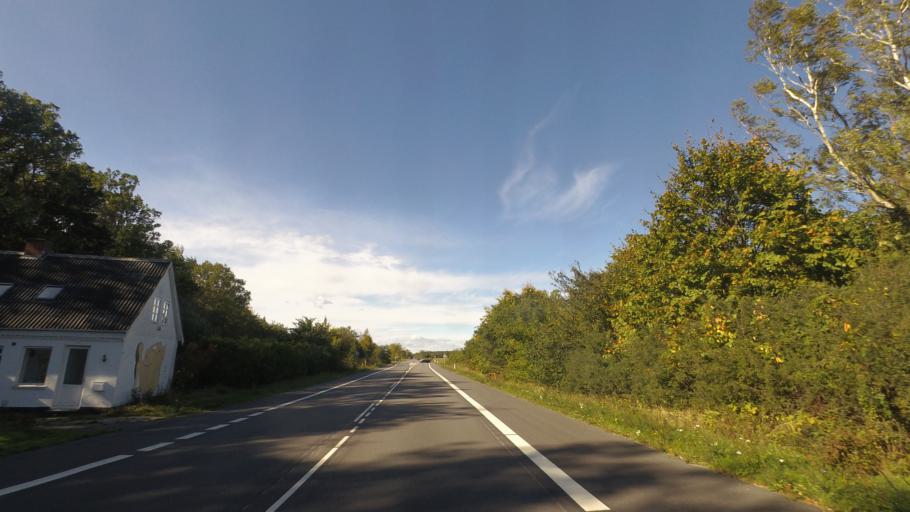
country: DK
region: Capital Region
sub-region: Bornholm Kommune
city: Ronne
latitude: 55.0858
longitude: 14.7465
